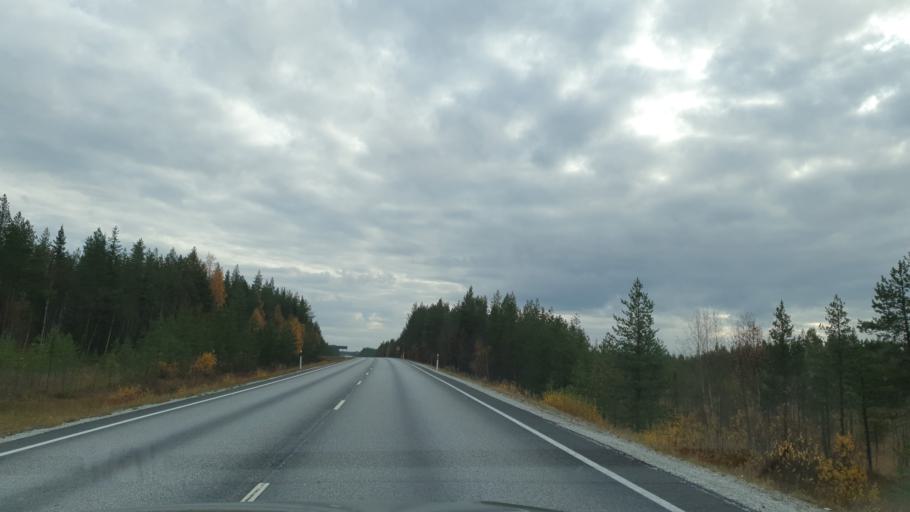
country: FI
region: Northern Ostrobothnia
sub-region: Oulunkaari
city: Pudasjaervi
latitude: 65.4155
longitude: 26.8809
